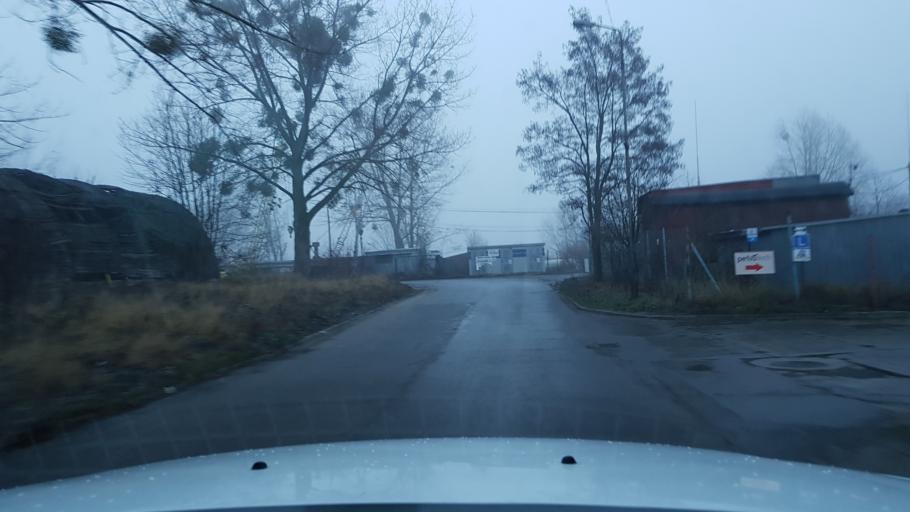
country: PL
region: West Pomeranian Voivodeship
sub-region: Powiat policki
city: Przeclaw
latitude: 53.3882
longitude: 14.4928
